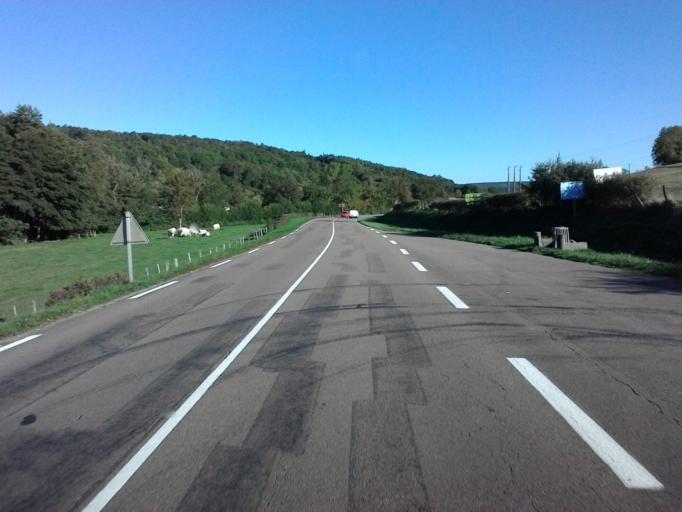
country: FR
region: Bourgogne
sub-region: Departement de la Cote-d'Or
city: Montbard
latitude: 47.6111
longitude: 4.3162
